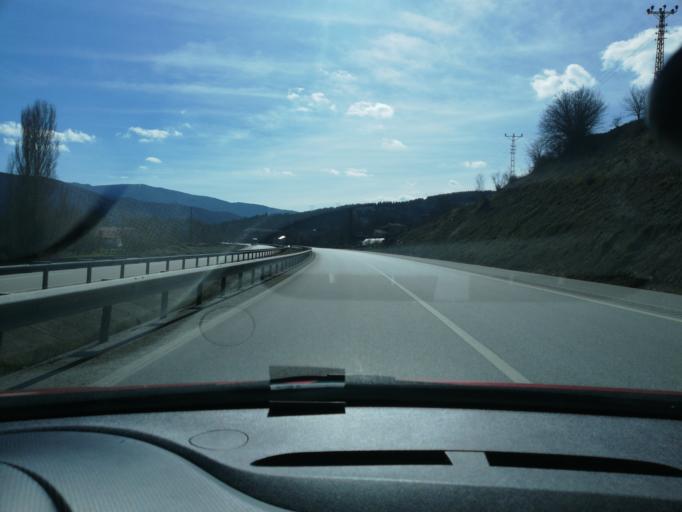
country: TR
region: Karabuk
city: Eskipazar
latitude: 41.0237
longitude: 32.6284
